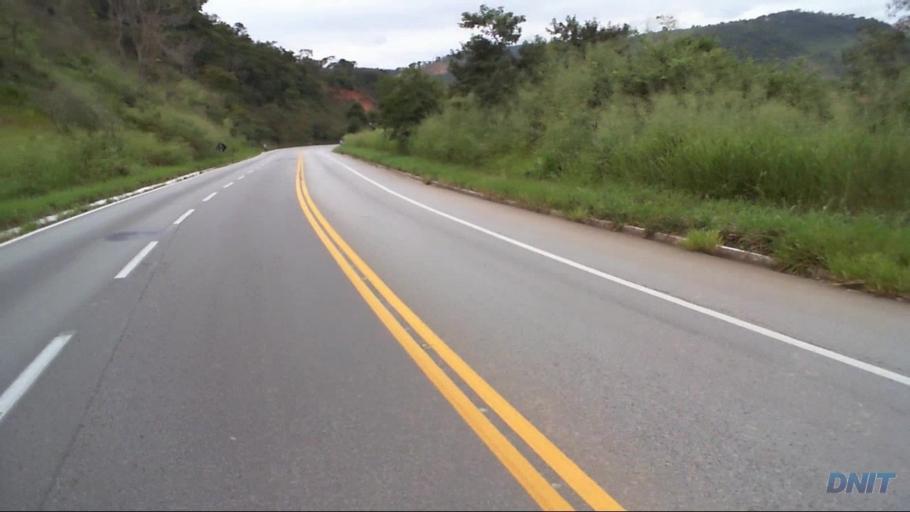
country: BR
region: Minas Gerais
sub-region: Nova Era
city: Nova Era
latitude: -19.7873
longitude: -43.0515
